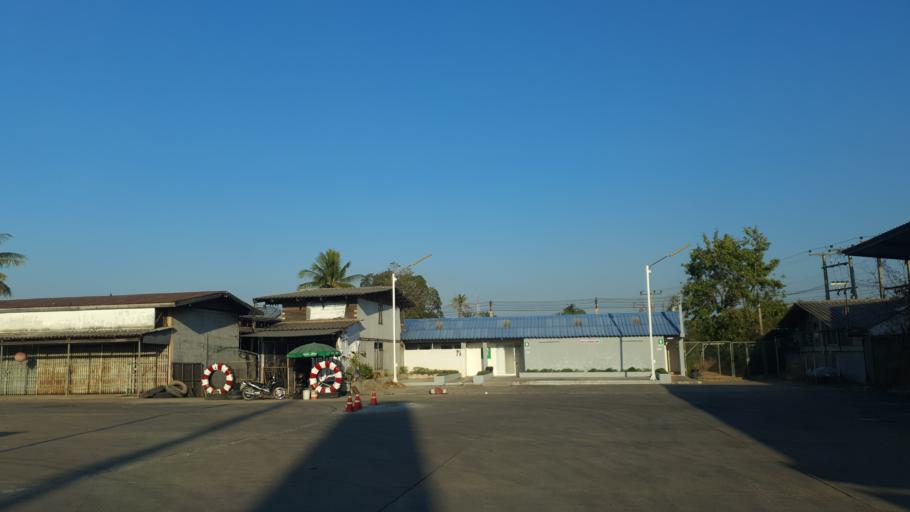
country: TH
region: Kamphaeng Phet
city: Khlong Khlung
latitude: 16.2118
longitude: 99.7041
